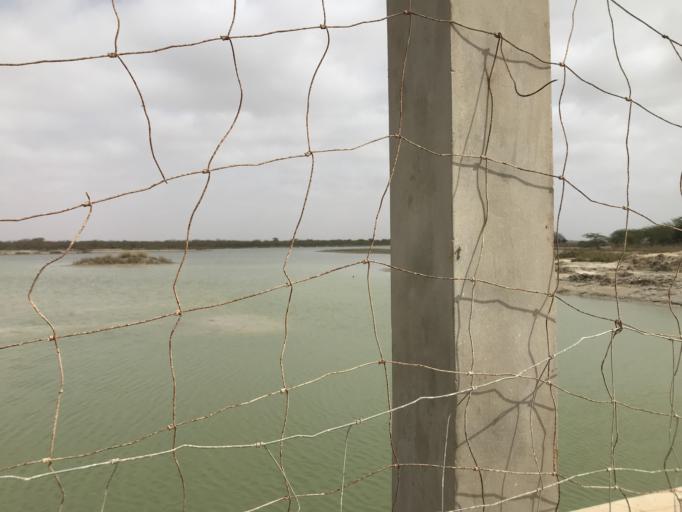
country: SN
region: Saint-Louis
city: Saint-Louis
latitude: 15.9302
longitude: -16.4573
